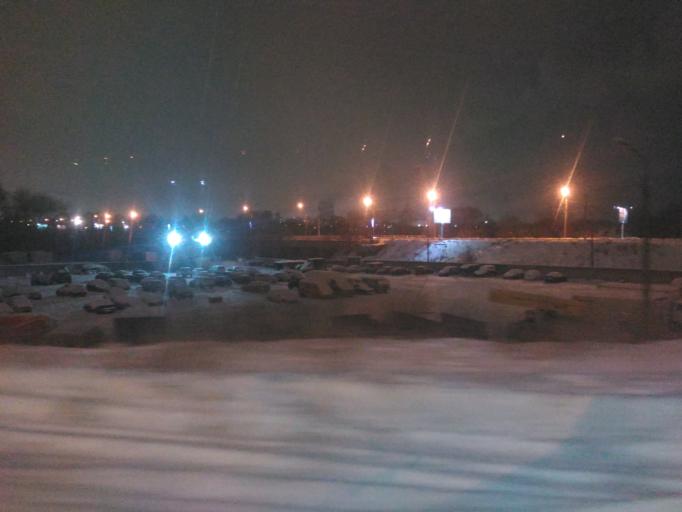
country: RU
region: Ulyanovsk
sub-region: Ulyanovskiy Rayon
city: Ulyanovsk
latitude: 54.3267
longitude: 48.3592
